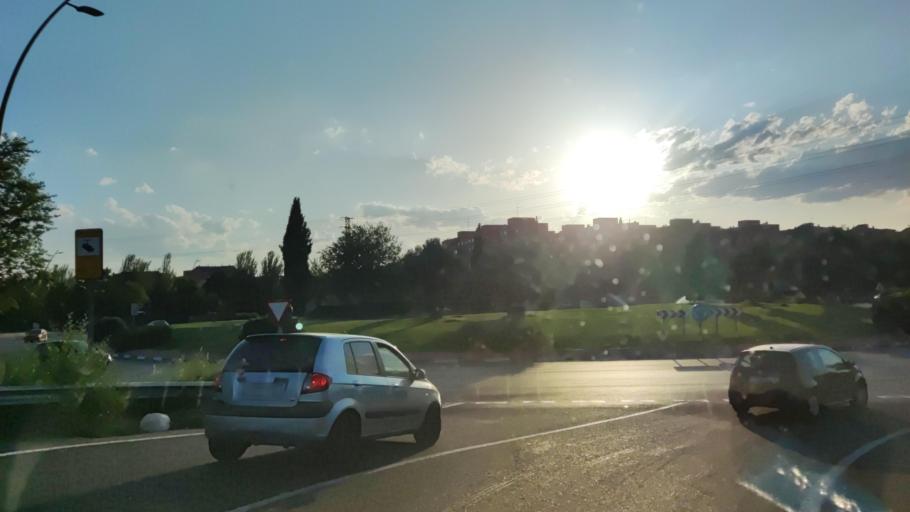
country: ES
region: Madrid
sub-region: Provincia de Madrid
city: Leganes
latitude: 40.3343
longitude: -3.7357
